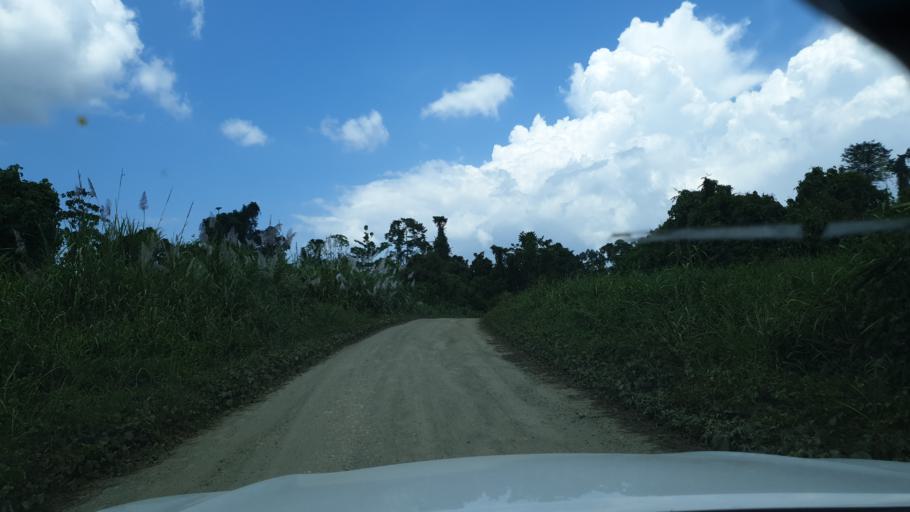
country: PG
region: East Sepik
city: Angoram
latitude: -3.8972
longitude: 143.9180
